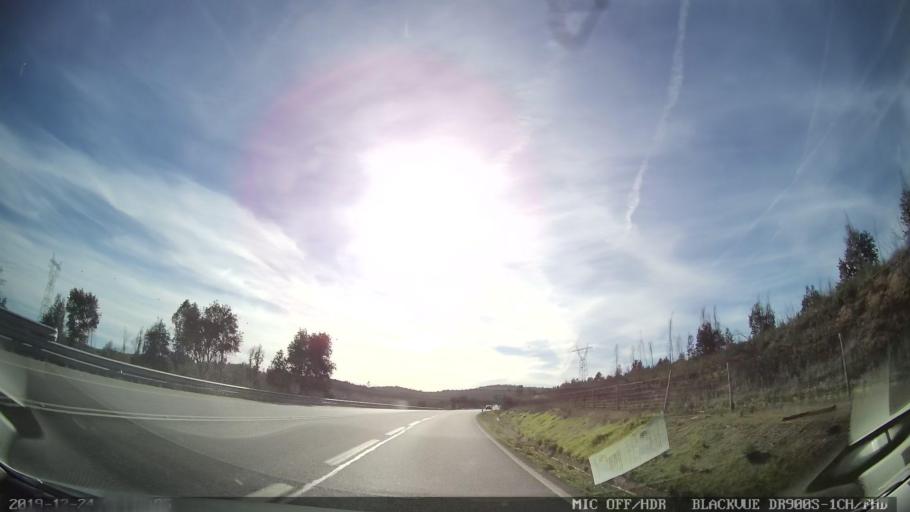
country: PT
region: Portalegre
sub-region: Nisa
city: Nisa
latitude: 39.5136
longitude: -7.7687
